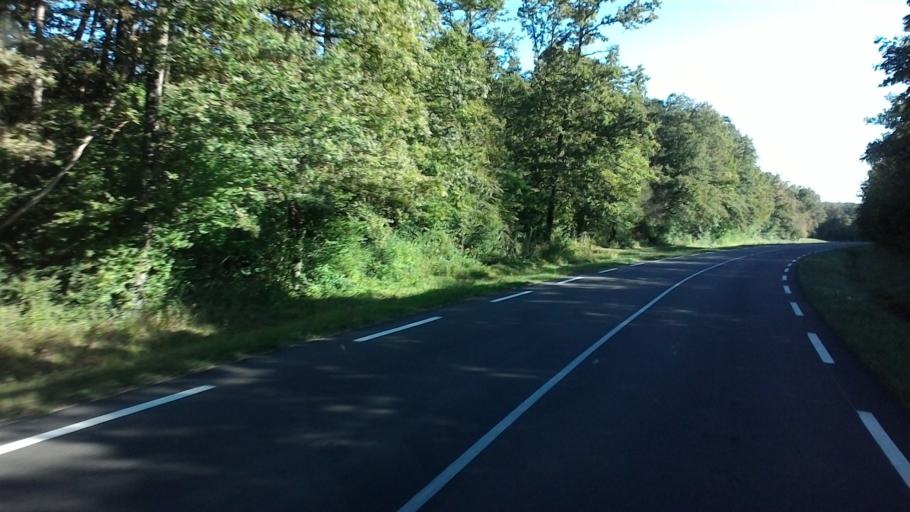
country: FR
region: Bourgogne
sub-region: Departement de la Cote-d'Or
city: Montbard
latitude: 47.7221
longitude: 4.4510
